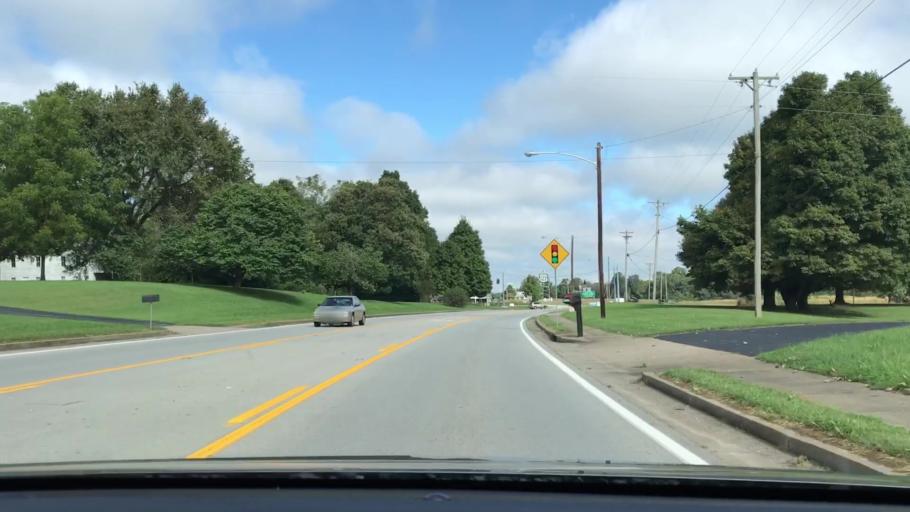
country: US
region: Kentucky
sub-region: Russell County
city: Jamestown
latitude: 36.9967
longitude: -85.0723
